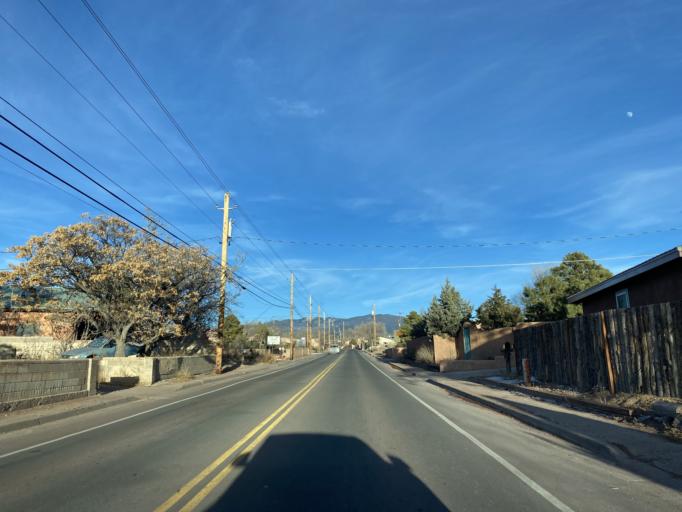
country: US
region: New Mexico
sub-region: Santa Fe County
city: Santa Fe
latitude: 35.6791
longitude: -105.9670
